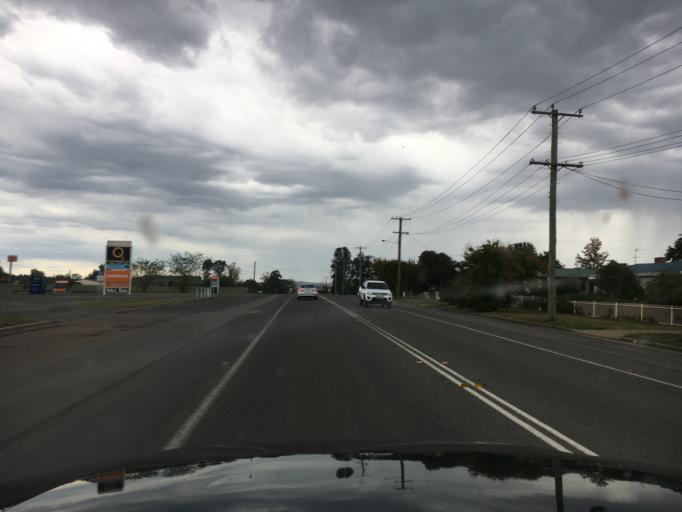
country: AU
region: New South Wales
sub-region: Muswellbrook
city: Muswellbrook
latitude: -32.1723
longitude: 150.8906
